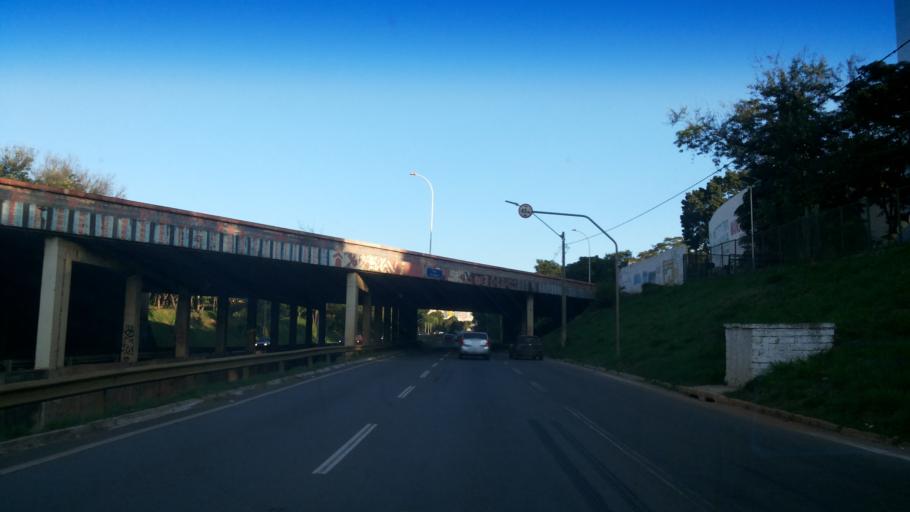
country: BR
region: Goias
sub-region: Goiania
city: Goiania
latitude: -16.6629
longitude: -49.2524
